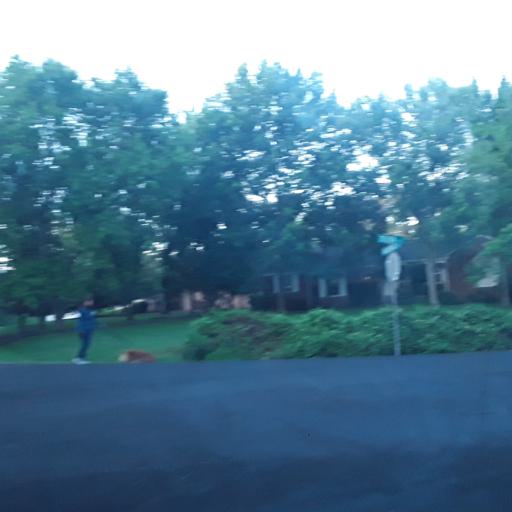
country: US
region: Tennessee
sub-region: Davidson County
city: Oak Hill
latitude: 36.0634
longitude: -86.7655
